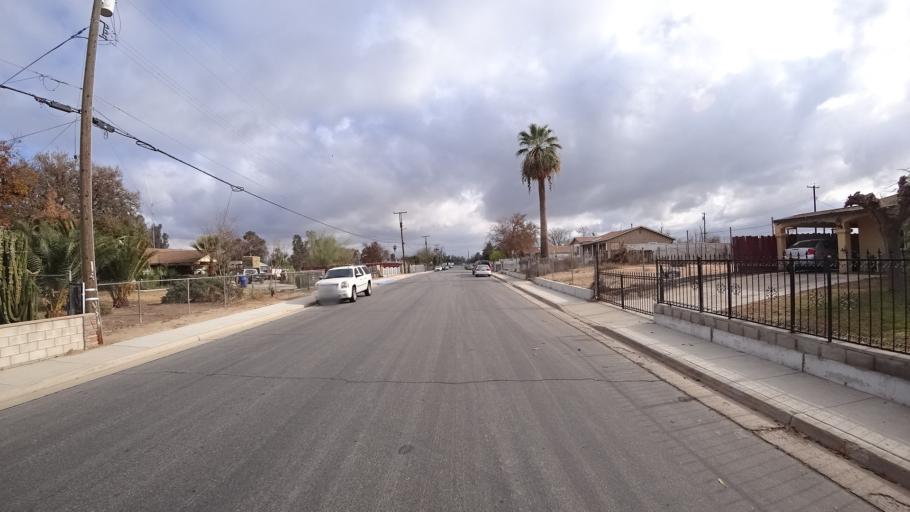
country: US
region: California
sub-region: Kern County
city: Bakersfield
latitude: 35.3344
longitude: -118.9882
